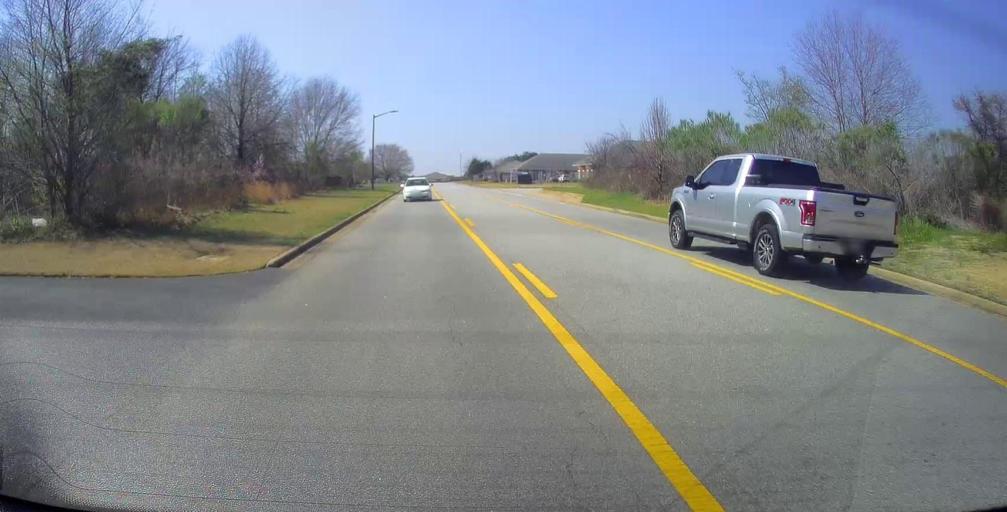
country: US
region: Georgia
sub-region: Houston County
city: Centerville
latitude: 32.6130
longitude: -83.6972
